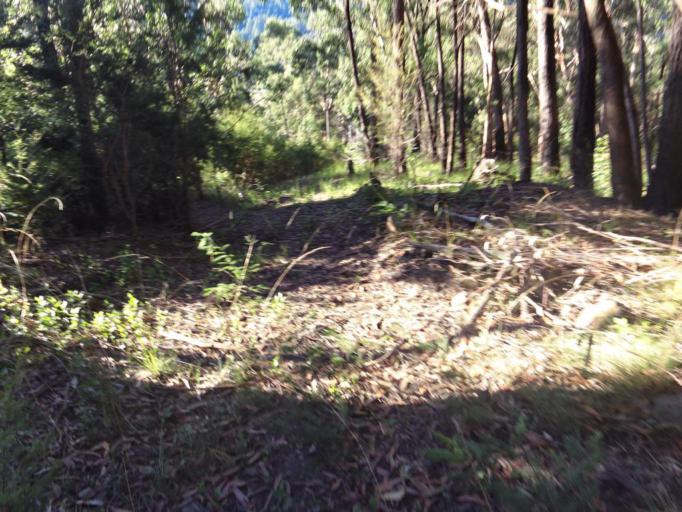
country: AU
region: Victoria
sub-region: Yarra Ranges
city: Millgrove
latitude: -37.7573
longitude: 145.6693
